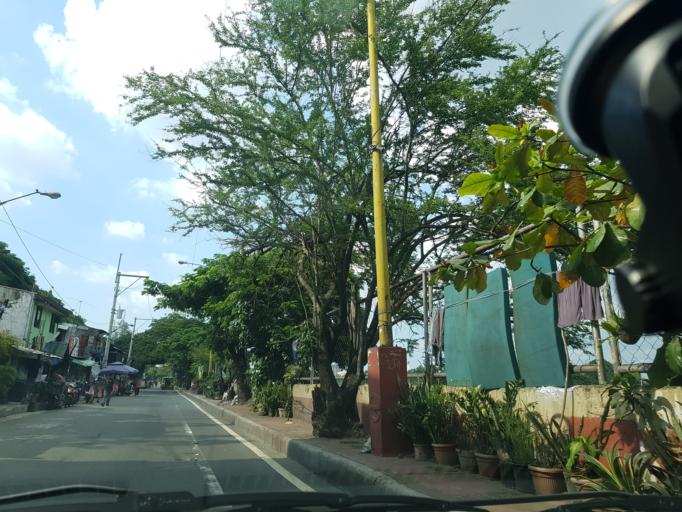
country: PH
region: Metro Manila
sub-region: Marikina
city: Calumpang
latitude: 14.5932
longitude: 121.0913
